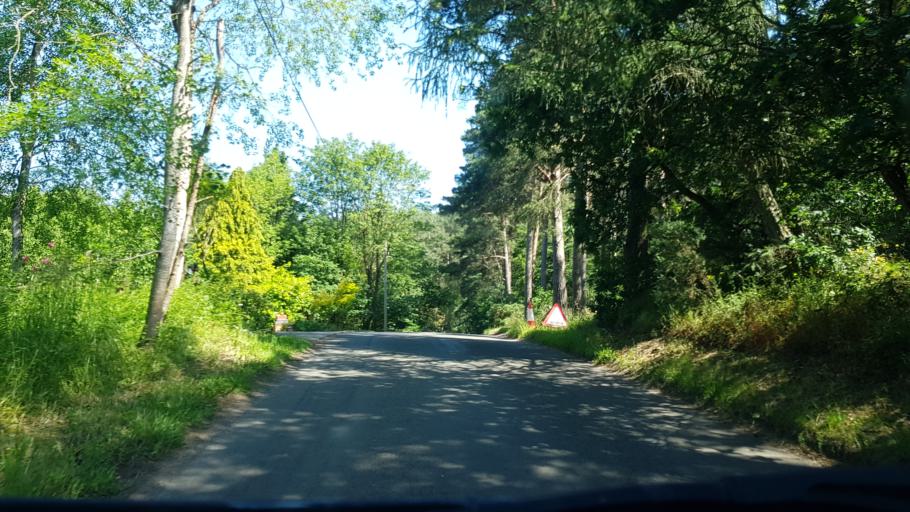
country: GB
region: England
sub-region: Worcestershire
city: Kidderminster
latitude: 52.4297
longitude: -2.2621
